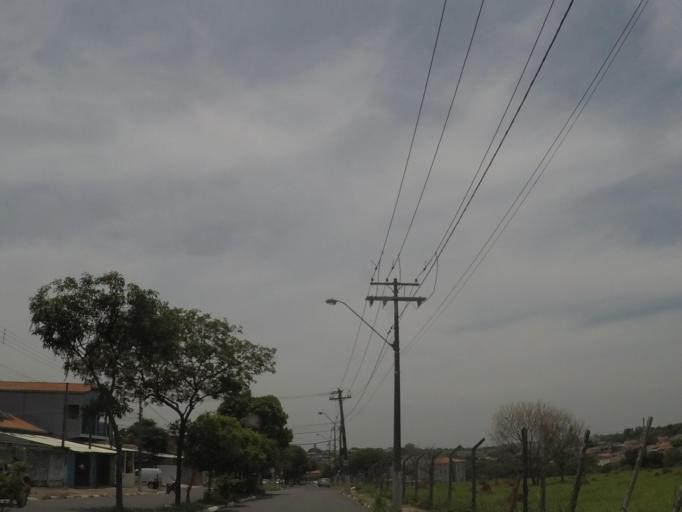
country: BR
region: Sao Paulo
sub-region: Hortolandia
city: Hortolandia
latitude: -22.8484
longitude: -47.1870
